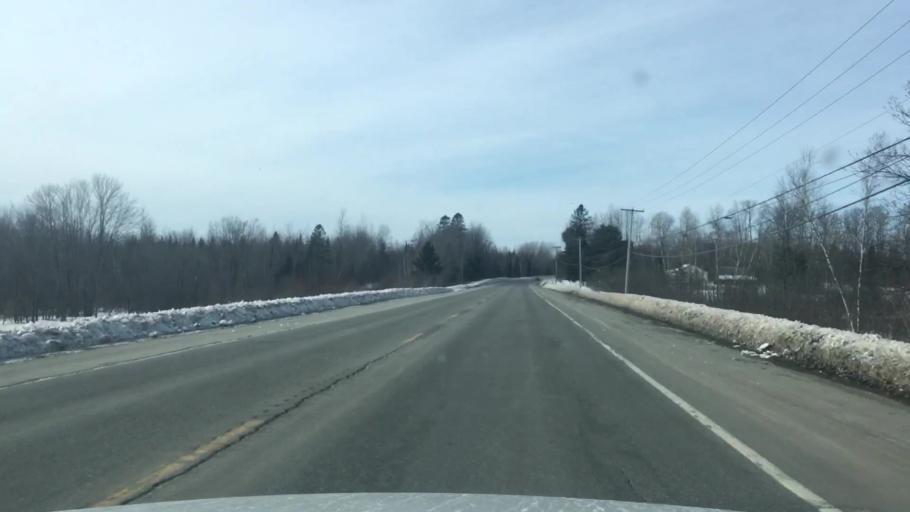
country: US
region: Maine
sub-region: Penobscot County
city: Kenduskeag
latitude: 44.9056
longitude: -68.8913
